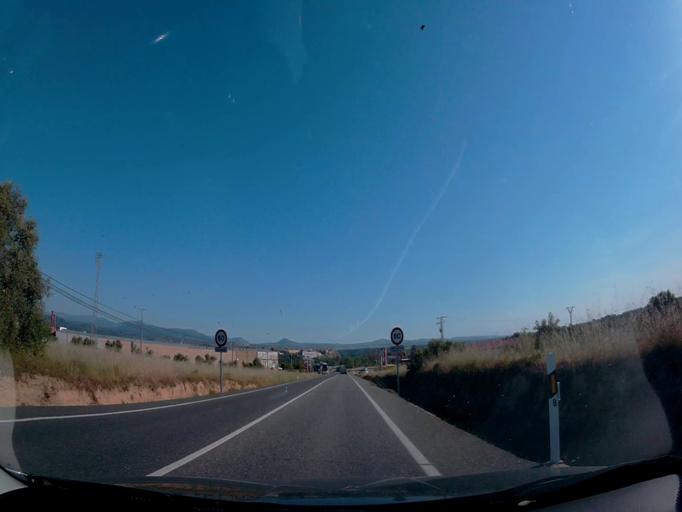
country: ES
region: Castille-La Mancha
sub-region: Province of Toledo
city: Escalona
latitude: 40.1468
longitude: -4.4028
